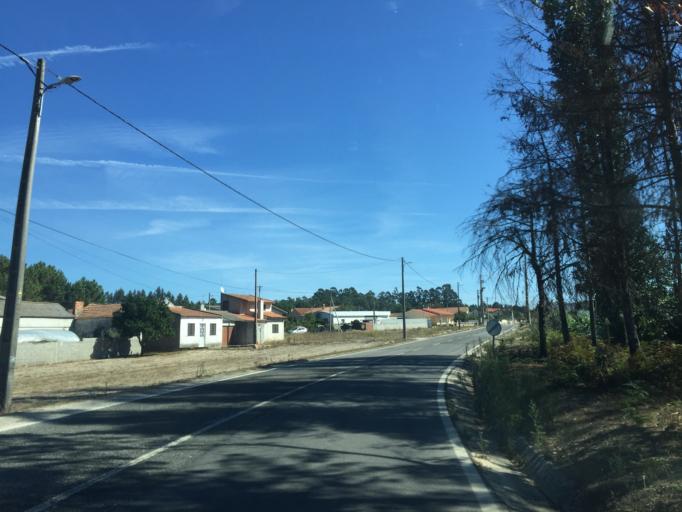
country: PT
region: Coimbra
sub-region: Figueira da Foz
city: Alhadas
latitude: 40.2221
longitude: -8.8220
